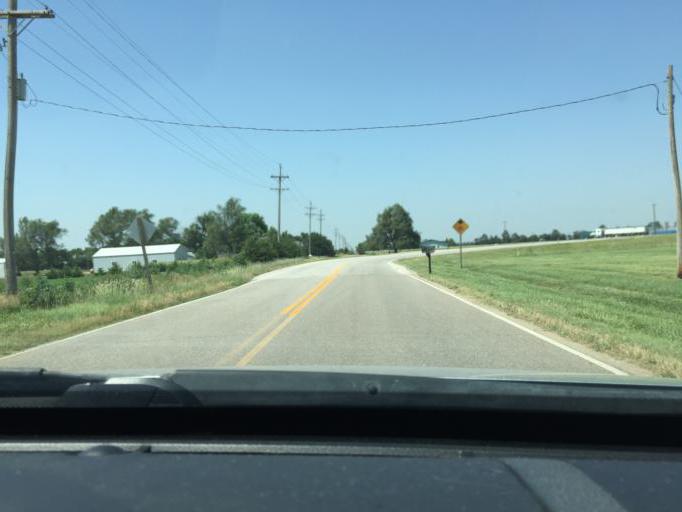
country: US
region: Kansas
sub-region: Reno County
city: South Hutchinson
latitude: 37.9425
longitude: -97.8852
